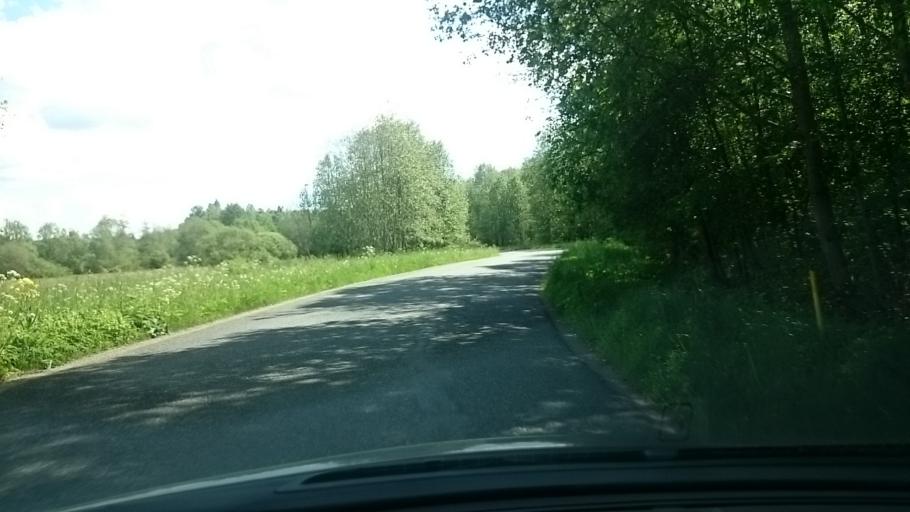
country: EE
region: Harju
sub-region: Anija vald
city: Kehra
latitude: 59.0991
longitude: 25.2956
